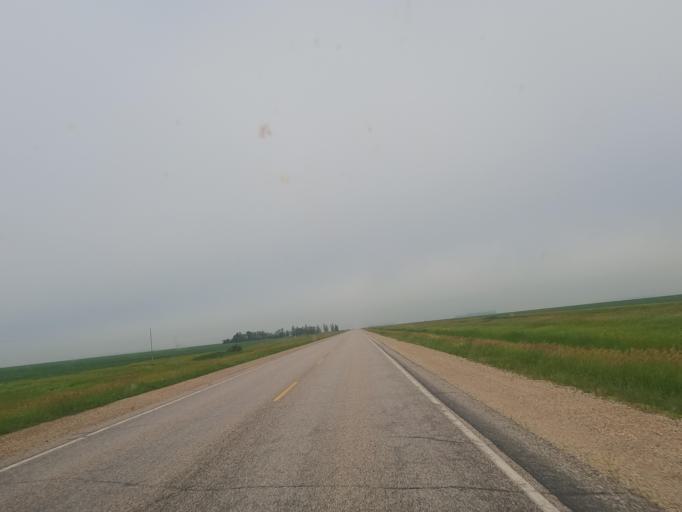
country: CA
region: Manitoba
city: Carman
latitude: 49.7376
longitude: -97.8383
